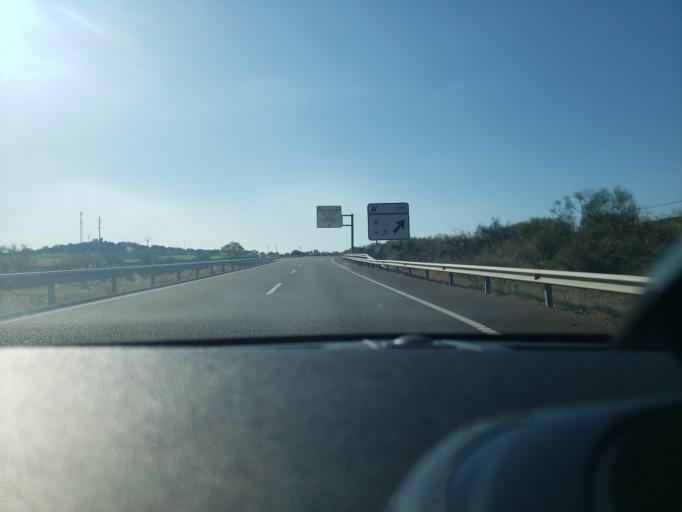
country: ES
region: Extremadura
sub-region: Provincia de Badajoz
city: San Pedro de Merida
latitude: 38.9483
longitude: -6.1735
